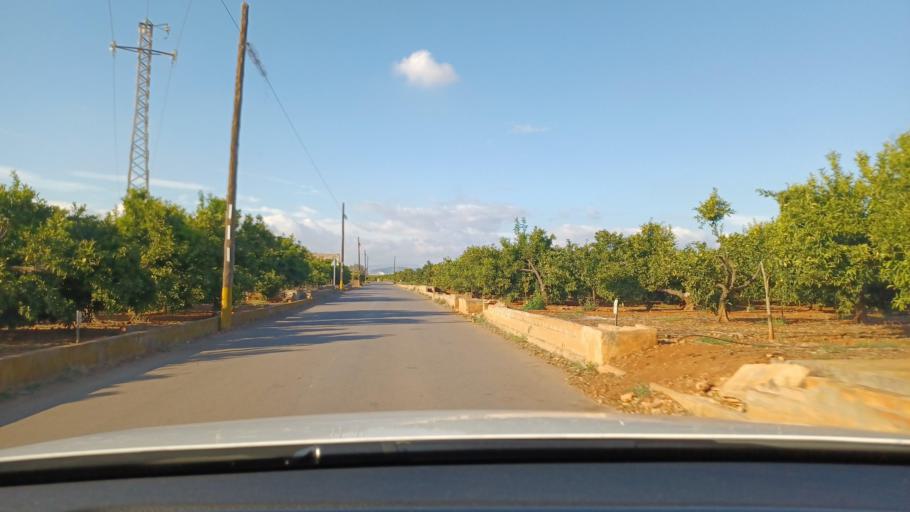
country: ES
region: Valencia
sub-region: Provincia de Castello
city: Betxi
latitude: 39.9387
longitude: -0.2097
